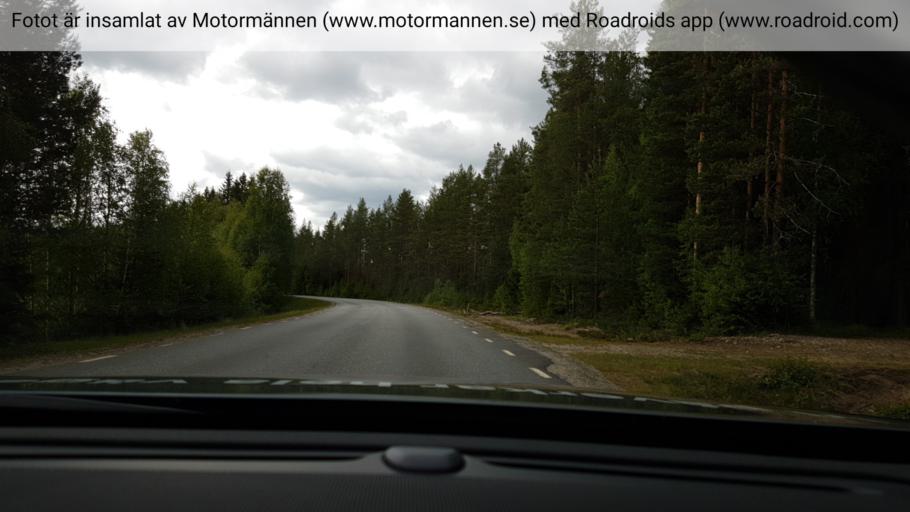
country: SE
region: Vaesterbotten
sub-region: Vindelns Kommun
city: Vindeln
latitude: 64.1847
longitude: 19.6819
